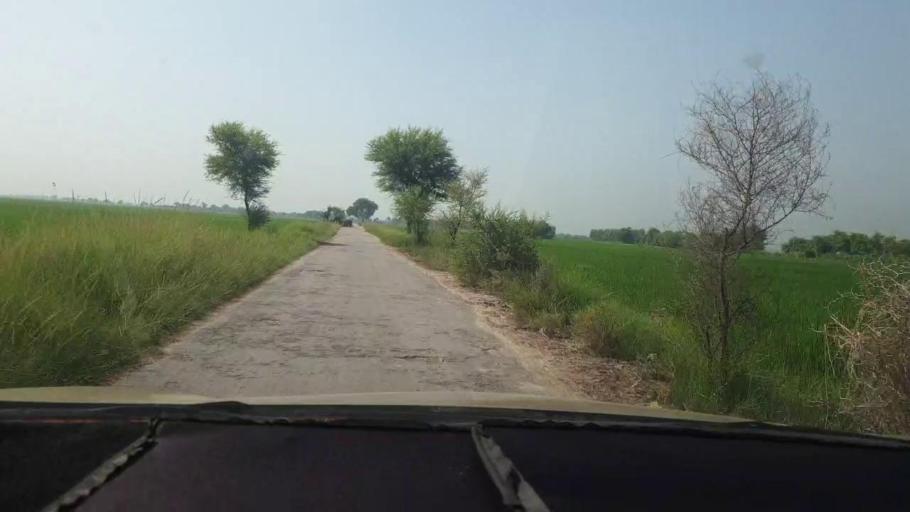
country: PK
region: Sindh
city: Kambar
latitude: 27.5788
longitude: 68.0555
